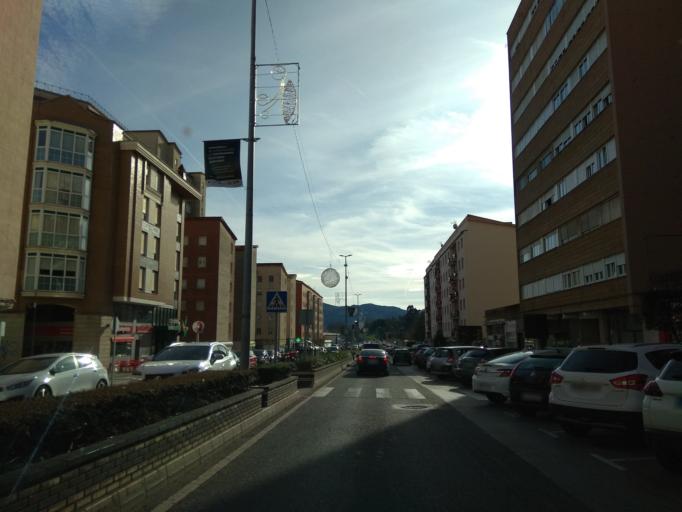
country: ES
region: Cantabria
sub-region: Provincia de Cantabria
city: El Astillero
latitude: 43.4170
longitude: -3.8453
